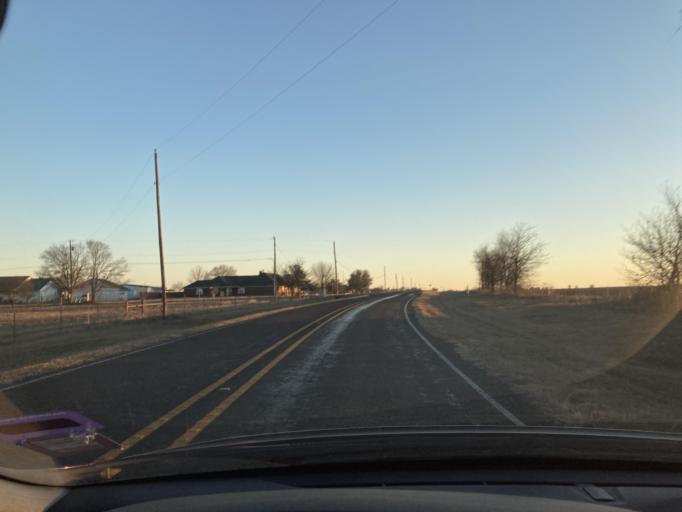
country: US
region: Texas
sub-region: Ellis County
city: Waxahachie
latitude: 32.3374
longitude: -96.8738
